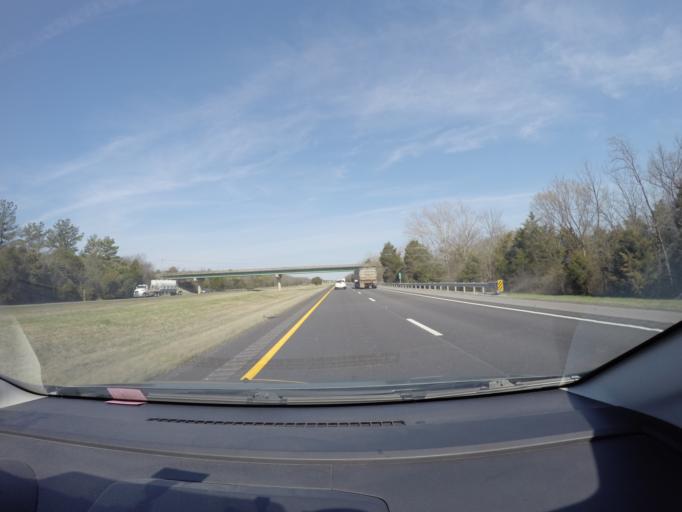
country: US
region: Tennessee
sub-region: Rutherford County
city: Plainview
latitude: 35.6708
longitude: -86.2803
